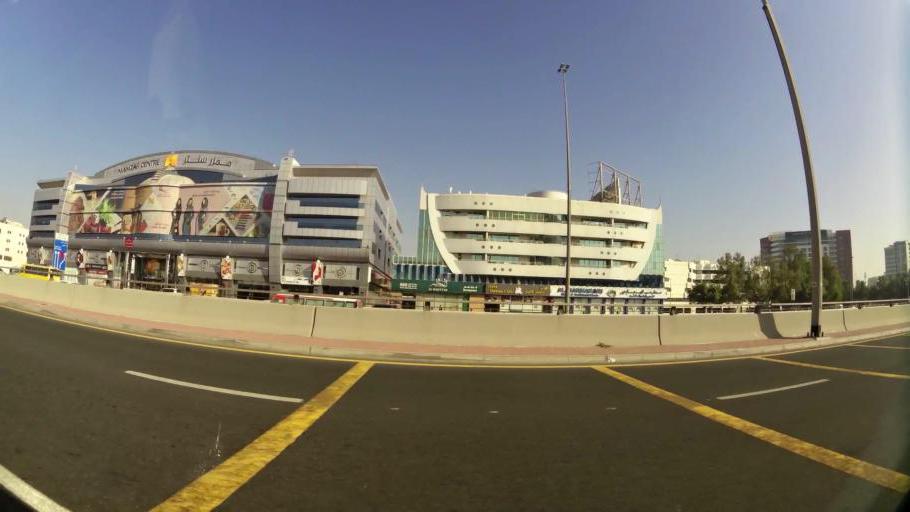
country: AE
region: Ash Shariqah
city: Sharjah
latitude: 25.2799
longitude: 55.3547
